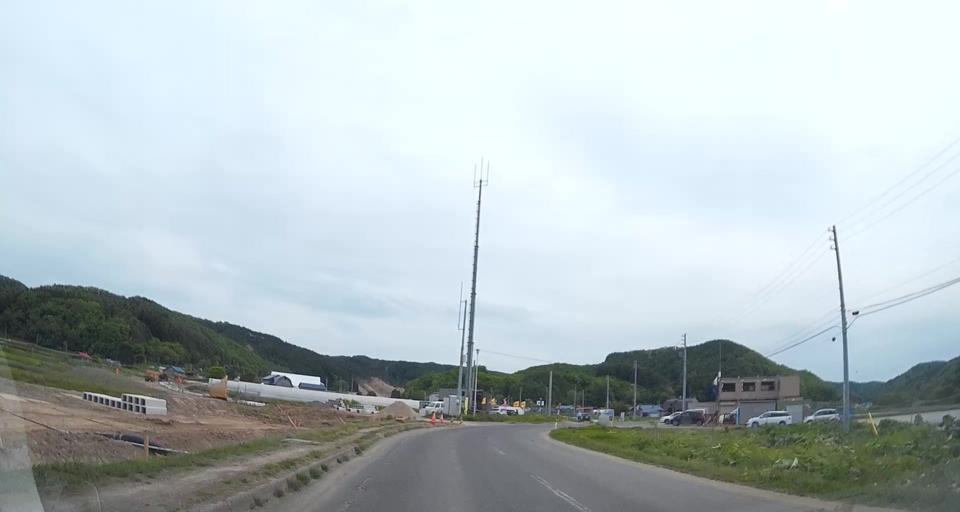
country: JP
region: Hokkaido
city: Chitose
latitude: 42.7556
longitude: 141.9736
